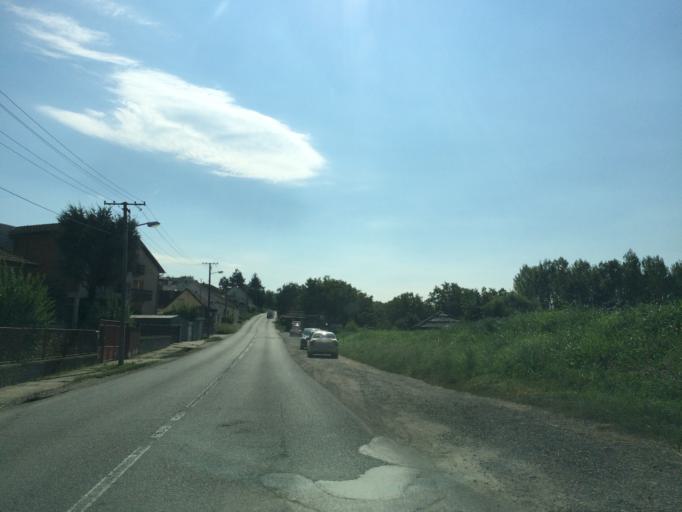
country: RS
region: Autonomna Pokrajina Vojvodina
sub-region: Juznobacki Okrug
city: Novi Sad
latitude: 45.2233
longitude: 19.8355
